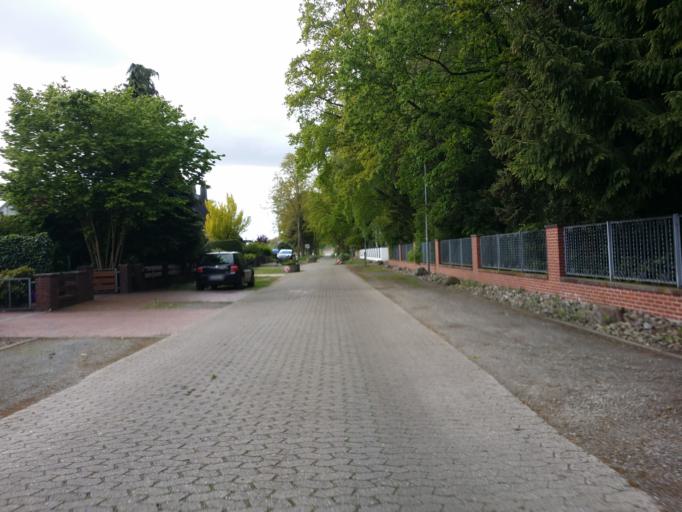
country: DE
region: Lower Saxony
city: Kirchseelte
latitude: 52.9898
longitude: 8.6877
